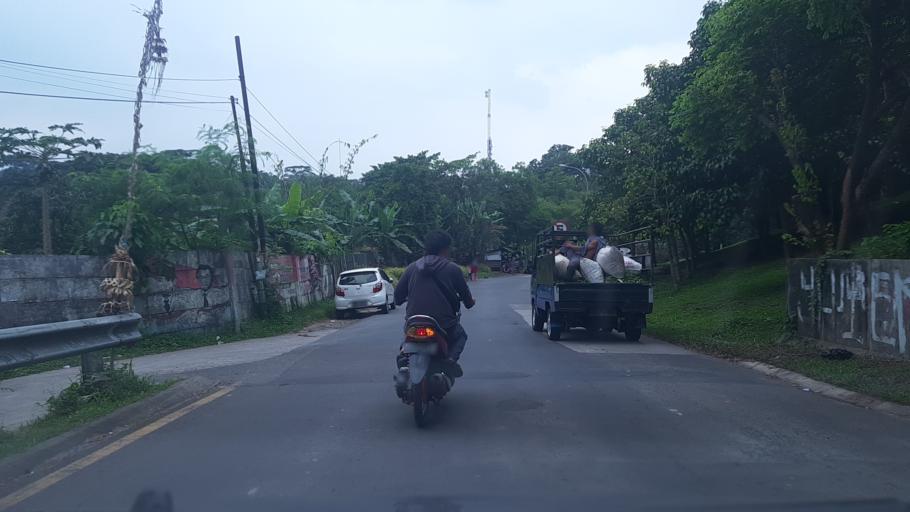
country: ID
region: West Java
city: Bogor
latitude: -6.5720
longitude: 106.8632
